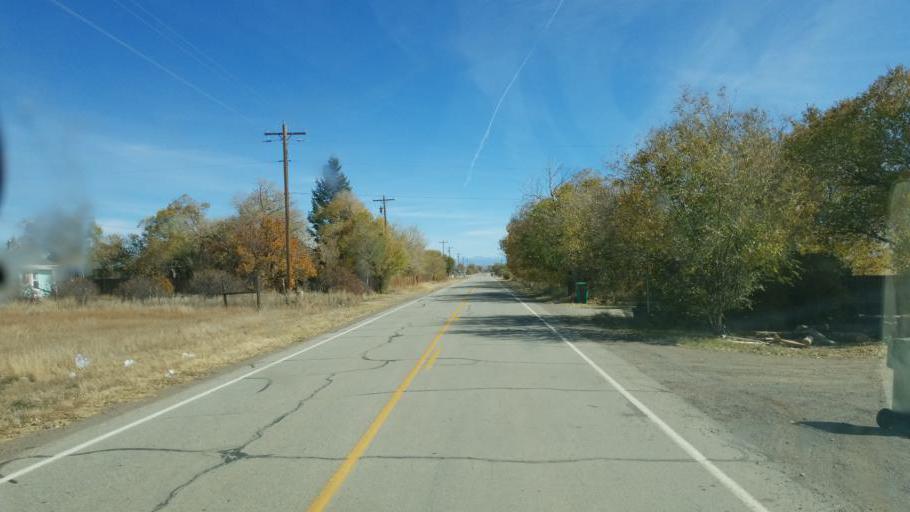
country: US
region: Colorado
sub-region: Conejos County
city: Conejos
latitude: 37.2835
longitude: -106.1072
